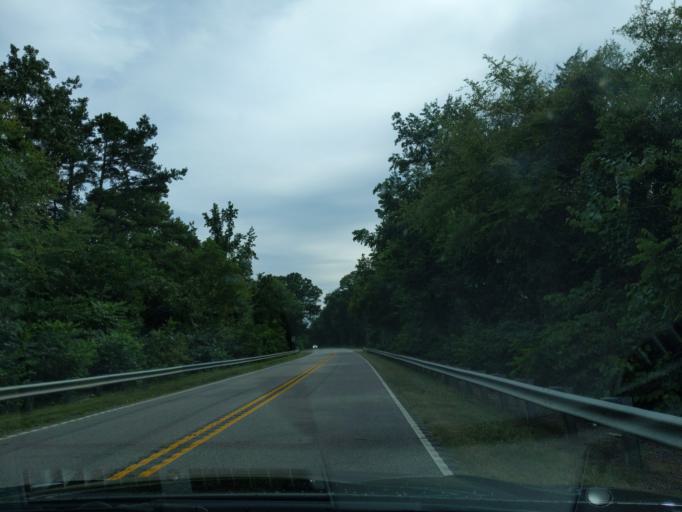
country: US
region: North Carolina
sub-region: Cabarrus County
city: Mount Pleasant
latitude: 35.4566
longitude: -80.3395
